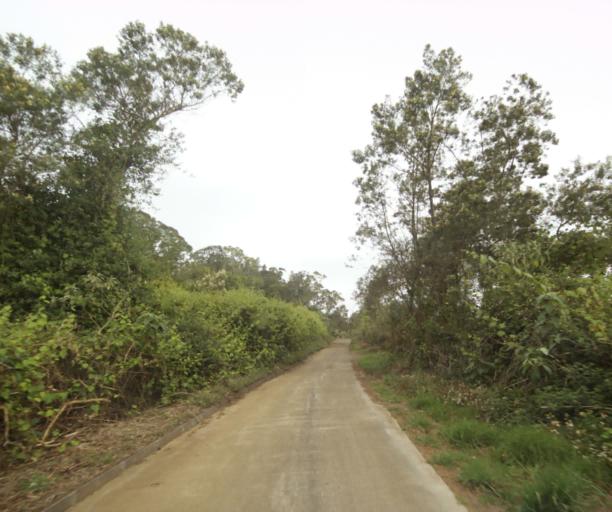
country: RE
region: Reunion
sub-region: Reunion
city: Saint-Paul
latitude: -21.0132
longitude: 55.3544
